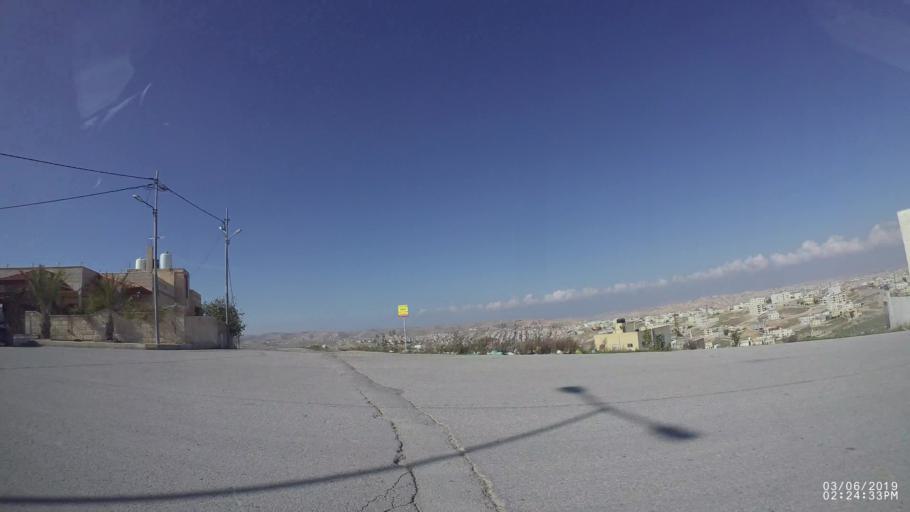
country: JO
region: Zarqa
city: Russeifa
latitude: 32.0428
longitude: 36.0396
